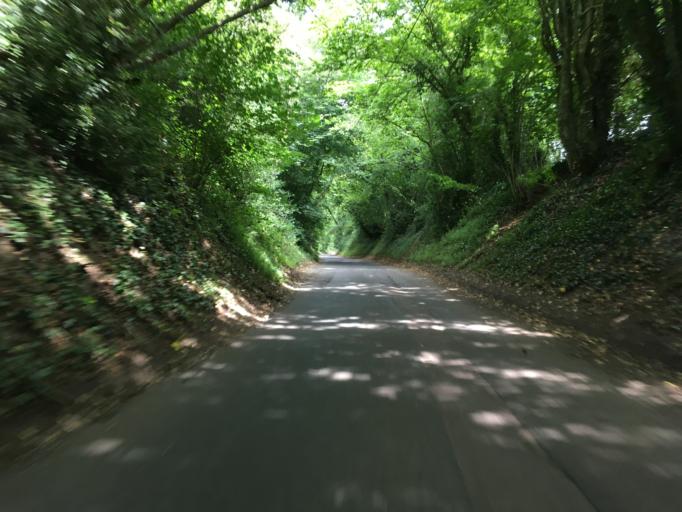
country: GB
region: England
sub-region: Hampshire
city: Highclere
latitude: 51.2669
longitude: -1.4191
